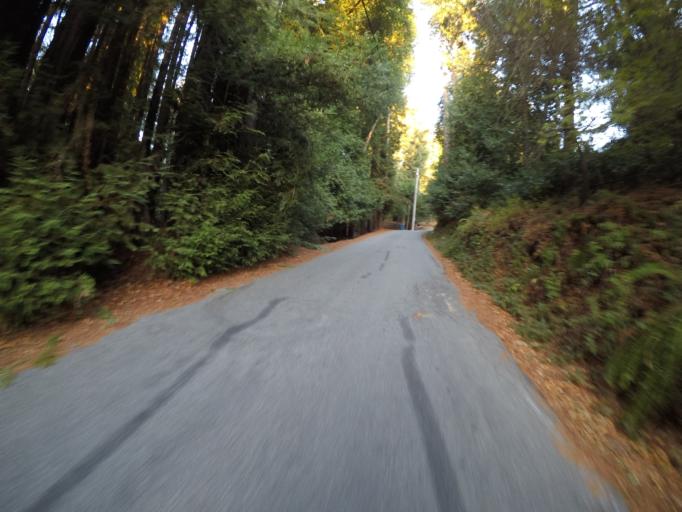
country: US
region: California
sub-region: Santa Cruz County
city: Scotts Valley
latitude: 37.0872
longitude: -122.0074
